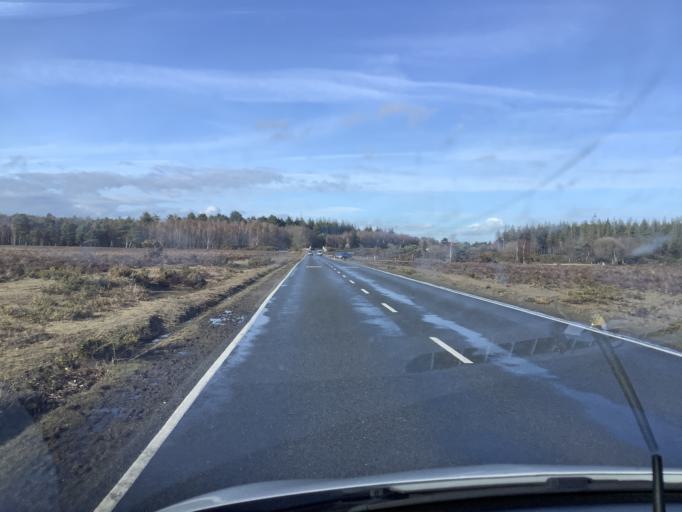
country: GB
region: England
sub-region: Hampshire
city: Hythe
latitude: 50.8440
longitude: -1.4247
